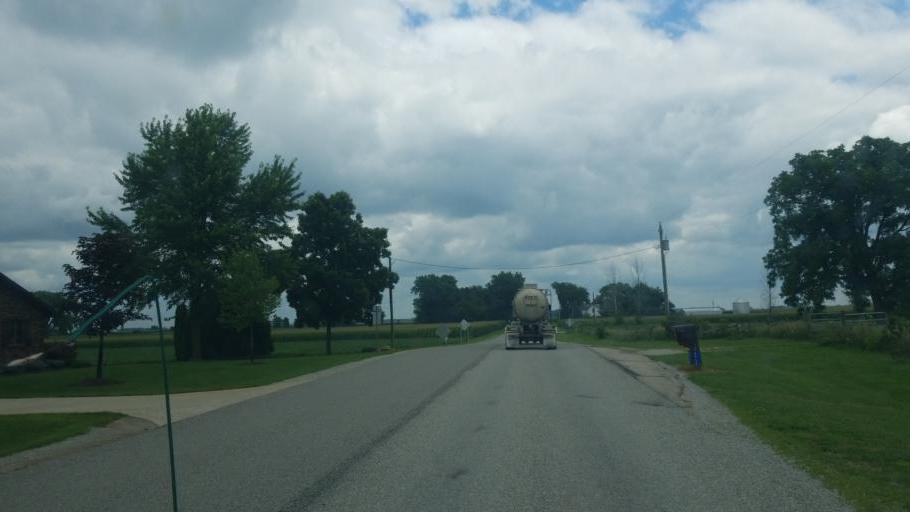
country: US
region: Indiana
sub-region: Wells County
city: Bluffton
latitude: 40.6550
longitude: -85.1473
